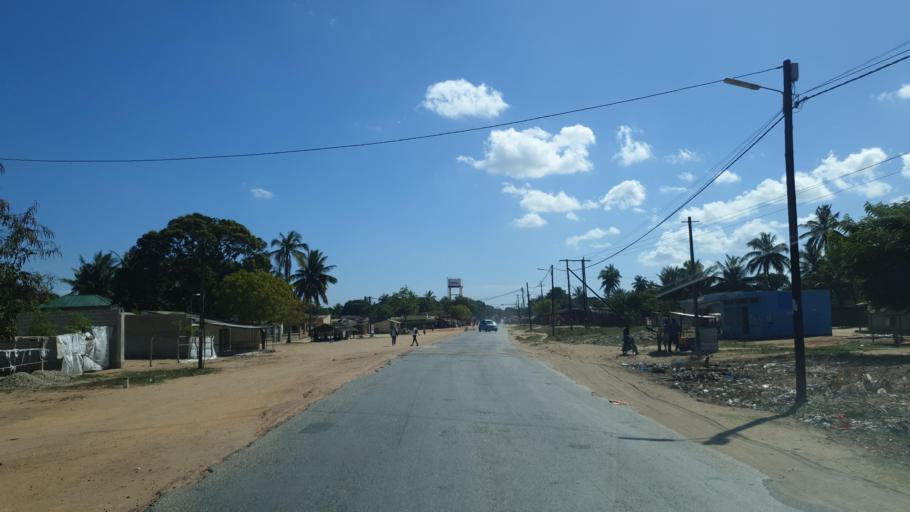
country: MZ
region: Nampula
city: Nacala
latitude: -14.5242
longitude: 40.6952
